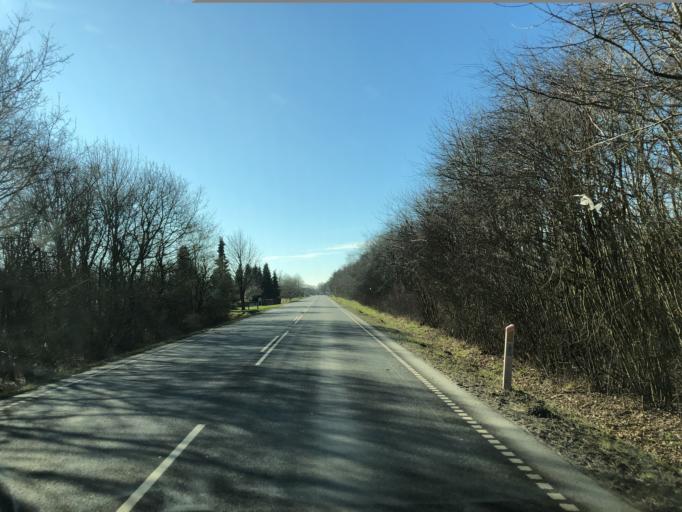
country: DK
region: Central Jutland
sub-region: Ikast-Brande Kommune
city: Bording Kirkeby
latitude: 56.1475
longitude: 9.2210
